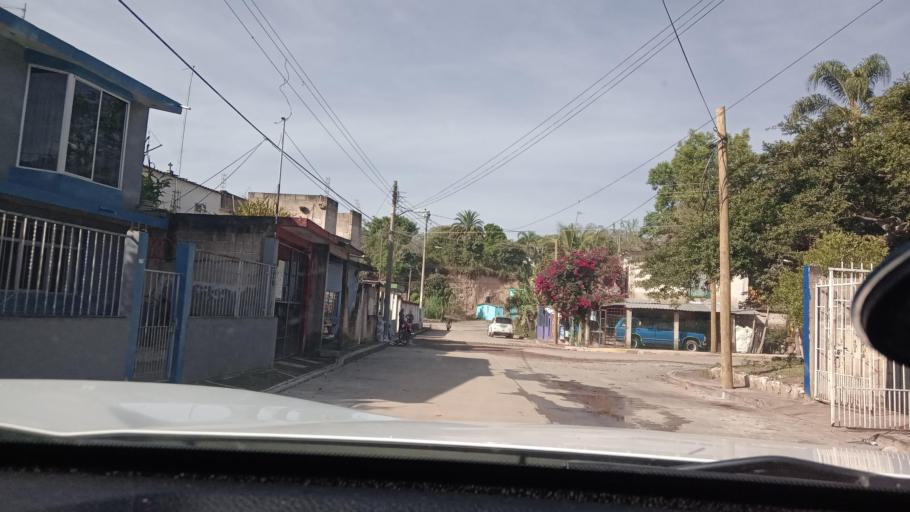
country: MX
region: Veracruz
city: El Castillo
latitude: 19.5644
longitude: -96.8616
